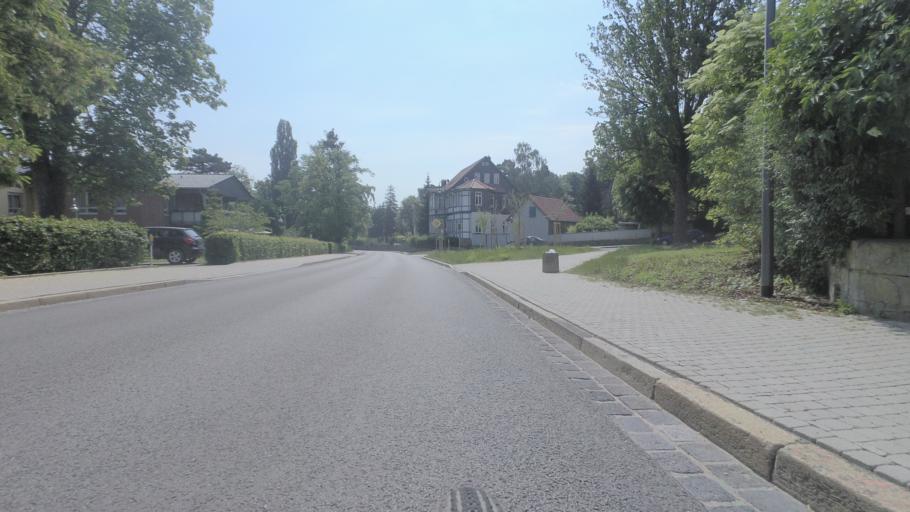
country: DE
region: Saxony-Anhalt
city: Blankenburg
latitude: 51.7920
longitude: 10.9485
